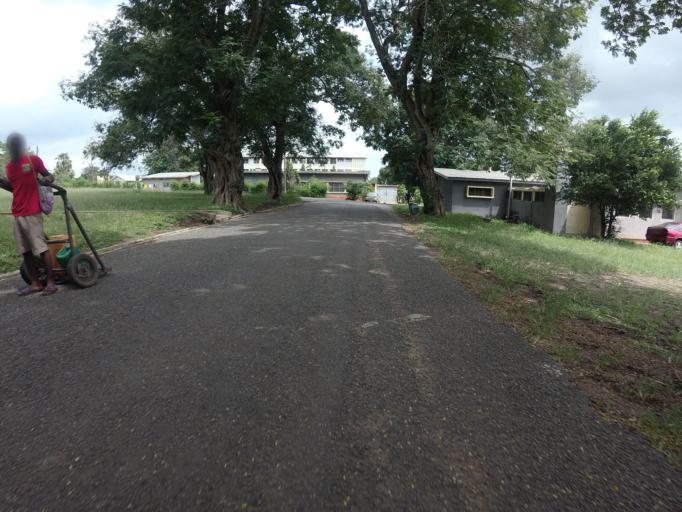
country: GH
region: Volta
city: Ho
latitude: 6.5963
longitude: 0.4744
